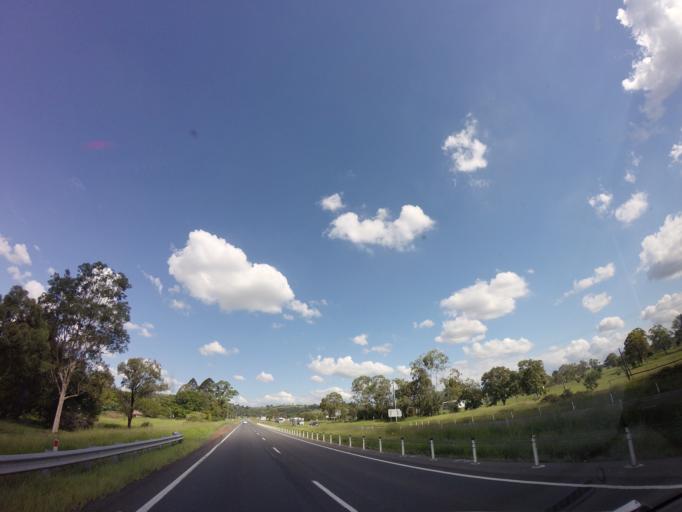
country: AU
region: Queensland
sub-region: Ipswich
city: Thagoona
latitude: -27.5540
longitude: 152.5410
